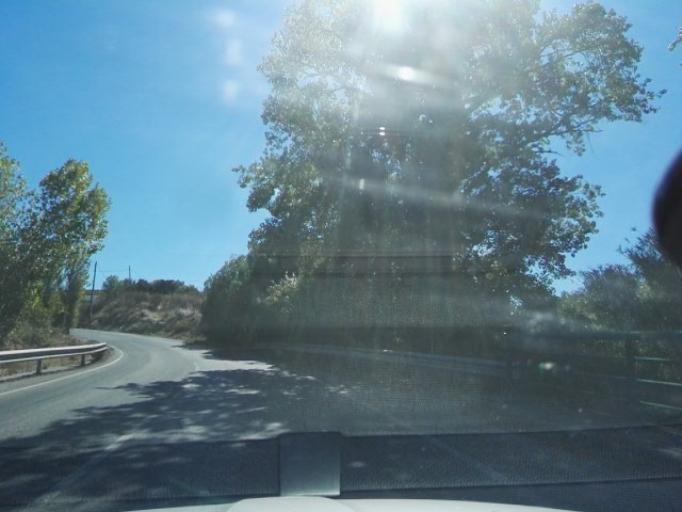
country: PT
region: Lisbon
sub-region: Arruda Dos Vinhos
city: Arruda dos Vinhos
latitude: 38.9773
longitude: -9.0754
